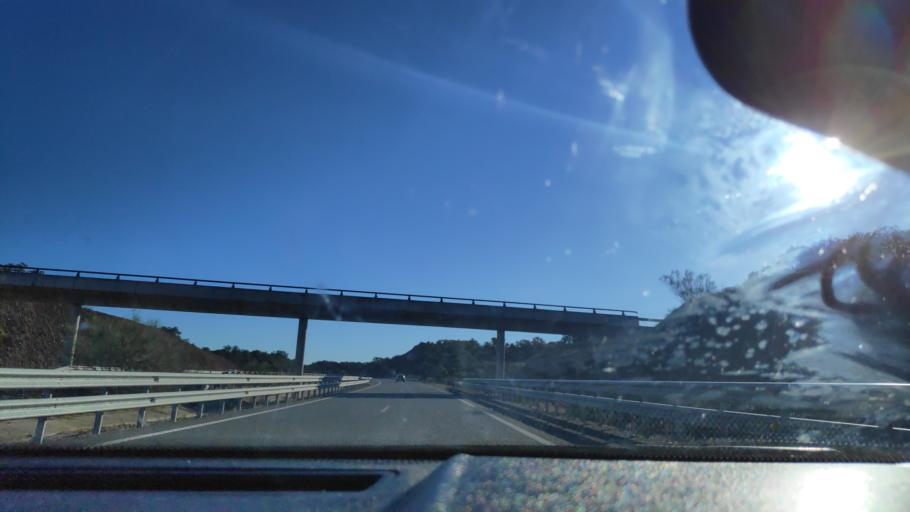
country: ES
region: Andalusia
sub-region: Provincia de Huelva
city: Santa Olalla del Cala
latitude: 37.8798
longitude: -6.2206
